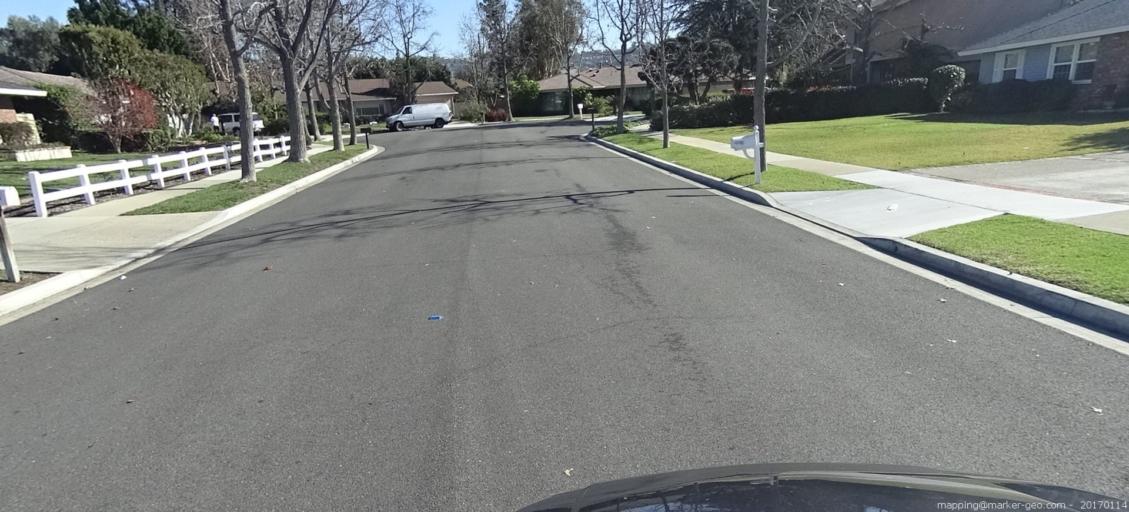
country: US
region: California
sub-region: Orange County
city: North Tustin
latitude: 33.7675
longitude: -117.8048
